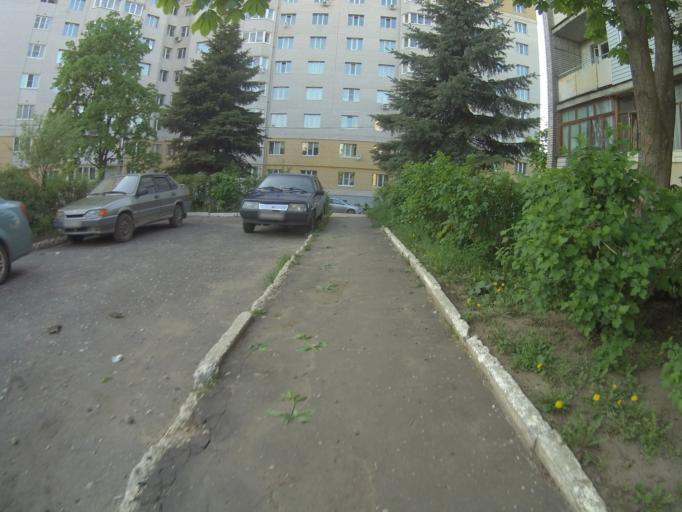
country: RU
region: Vladimir
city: Kommunar
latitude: 56.1697
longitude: 40.4600
